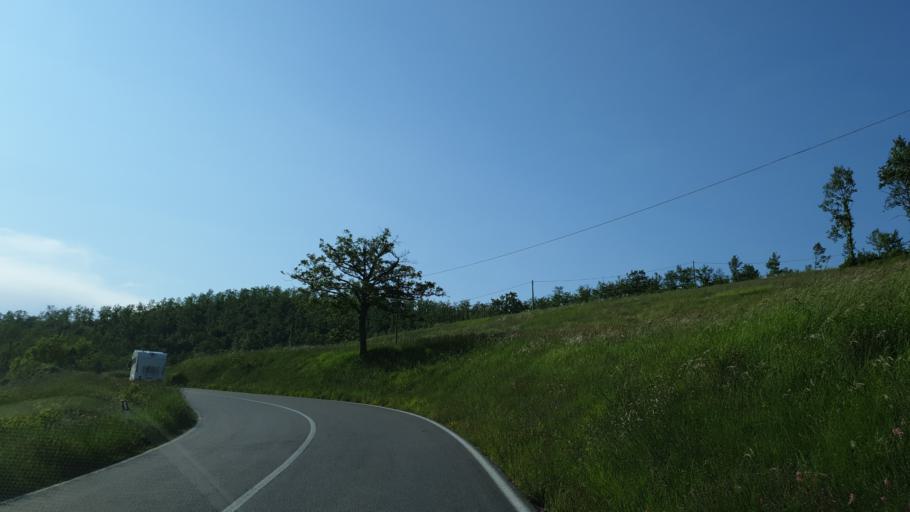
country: IT
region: Tuscany
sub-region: Province of Arezzo
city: Stia
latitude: 43.7770
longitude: 11.6843
